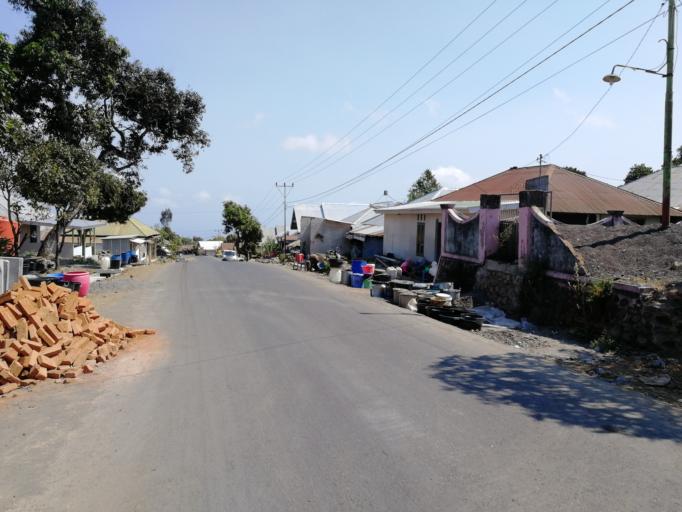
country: ID
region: West Nusa Tenggara
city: Lelongken
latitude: -8.3360
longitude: 116.4998
